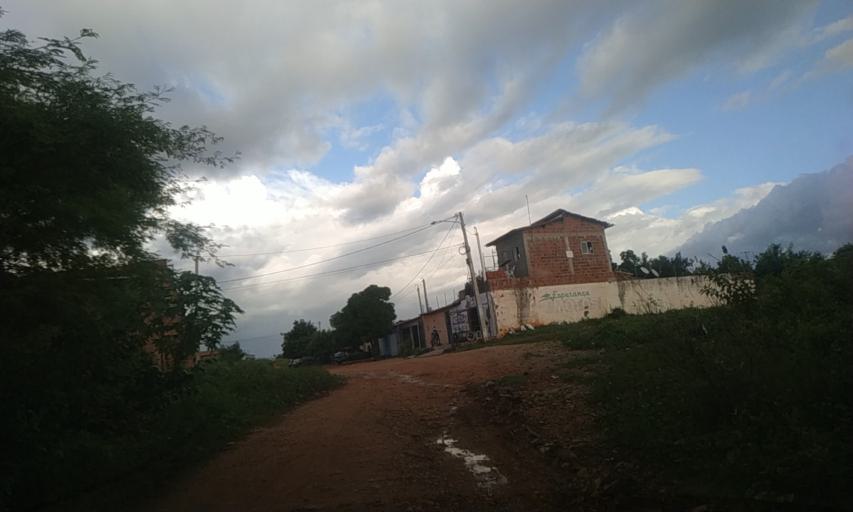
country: BR
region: Rio Grande do Norte
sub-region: Mossoro
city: Mossoro
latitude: -5.2179
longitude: -37.3478
